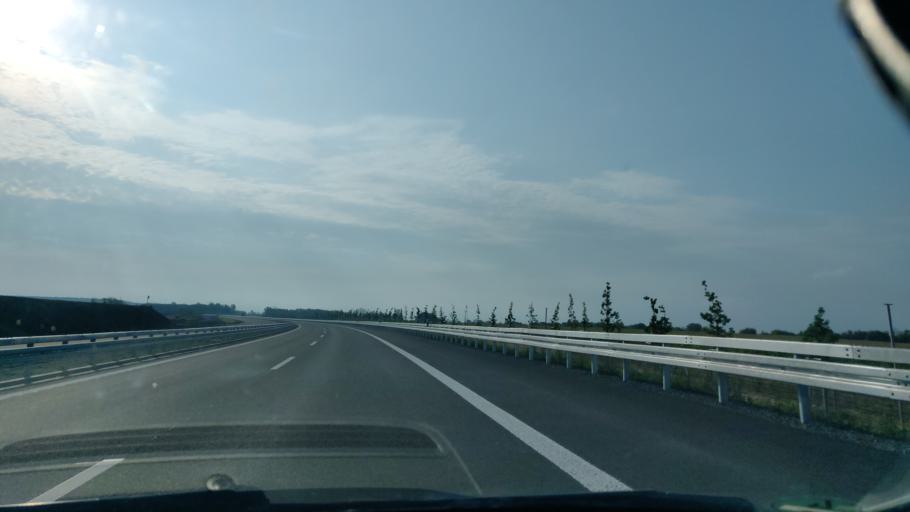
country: DE
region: Saxony
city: Espenhain
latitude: 51.1830
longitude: 12.4622
